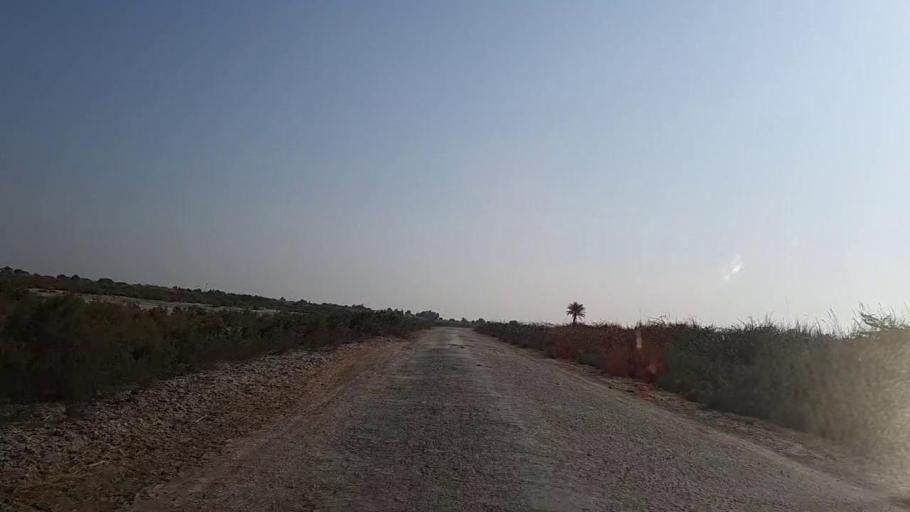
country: PK
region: Sindh
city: Tando Mittha Khan
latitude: 25.9059
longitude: 69.0770
